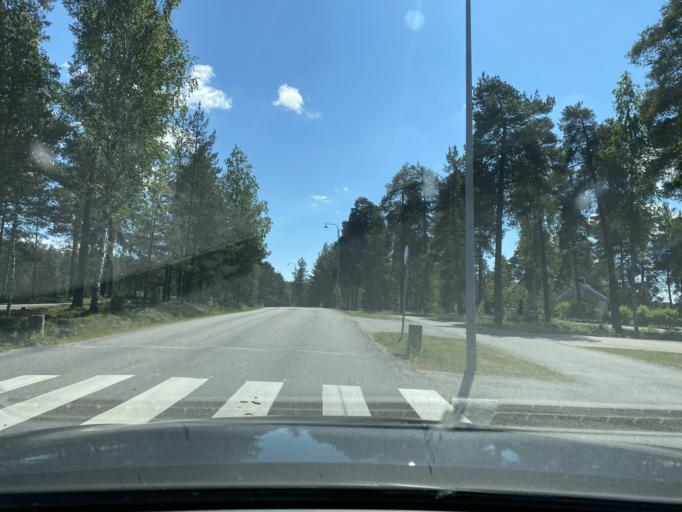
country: FI
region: Satakunta
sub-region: Rauma
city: Eura
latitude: 61.1198
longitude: 22.1597
